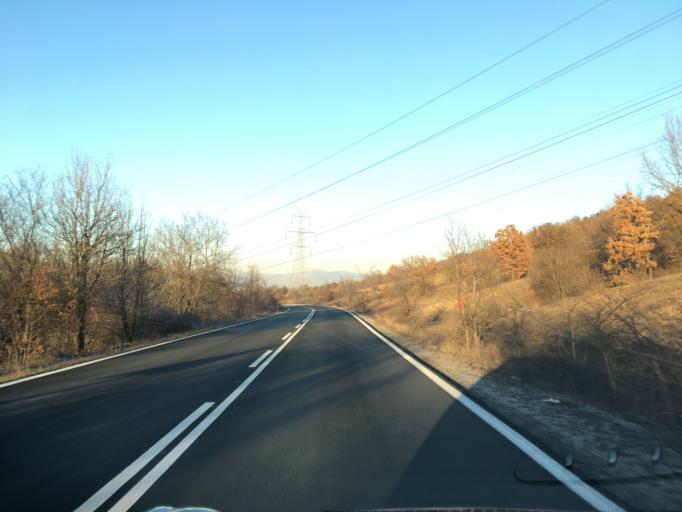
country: GR
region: West Macedonia
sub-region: Nomos Kozanis
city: Koila
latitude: 40.3189
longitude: 21.7651
